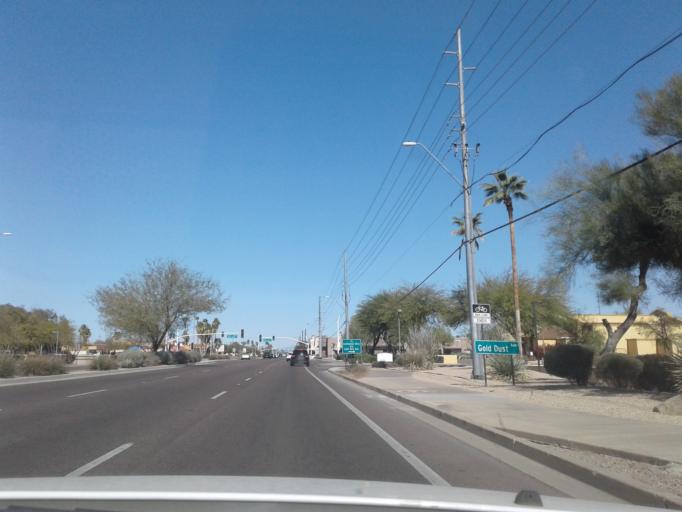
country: US
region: Arizona
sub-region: Maricopa County
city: Paradise Valley
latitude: 33.5774
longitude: -111.9257
